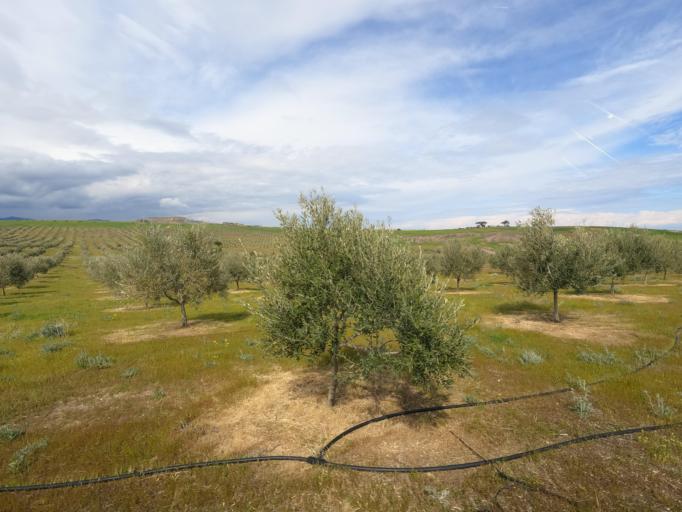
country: CY
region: Lefkosia
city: Lefka
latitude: 35.0905
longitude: 32.9287
